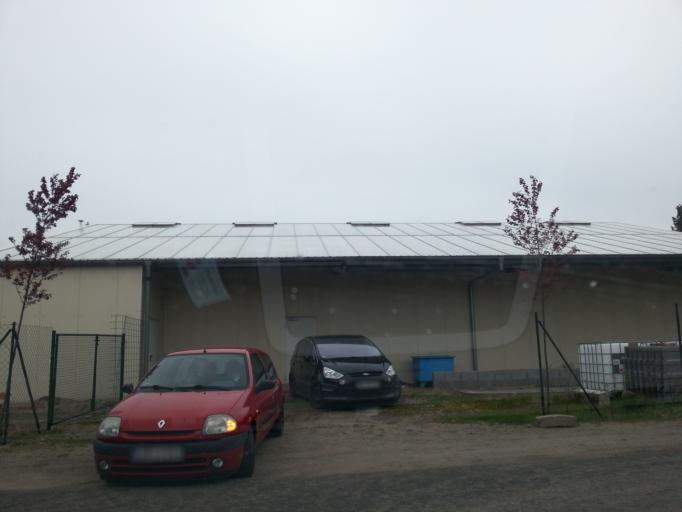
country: DE
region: Mecklenburg-Vorpommern
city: Malchow
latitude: 53.5128
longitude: 12.3549
